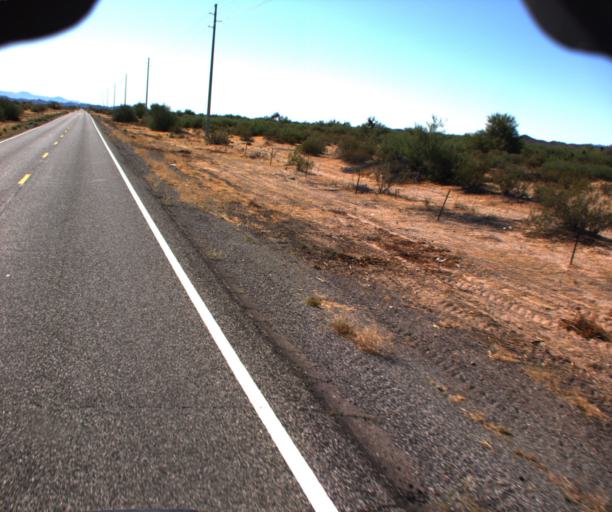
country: US
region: Arizona
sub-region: La Paz County
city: Cienega Springs
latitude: 33.9867
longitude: -114.0711
